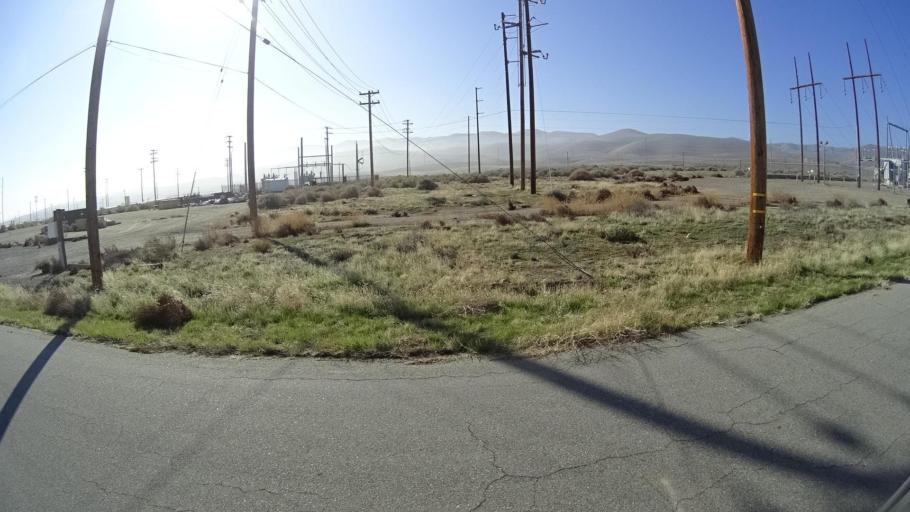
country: US
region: California
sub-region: Kern County
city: Taft Heights
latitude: 35.2267
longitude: -119.6299
